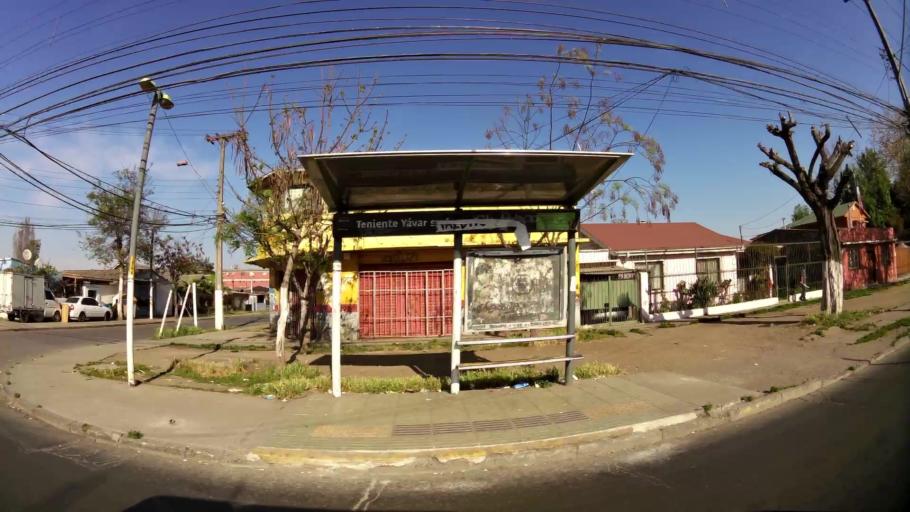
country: CL
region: Santiago Metropolitan
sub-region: Provincia de Santiago
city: Santiago
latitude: -33.3909
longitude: -70.6703
